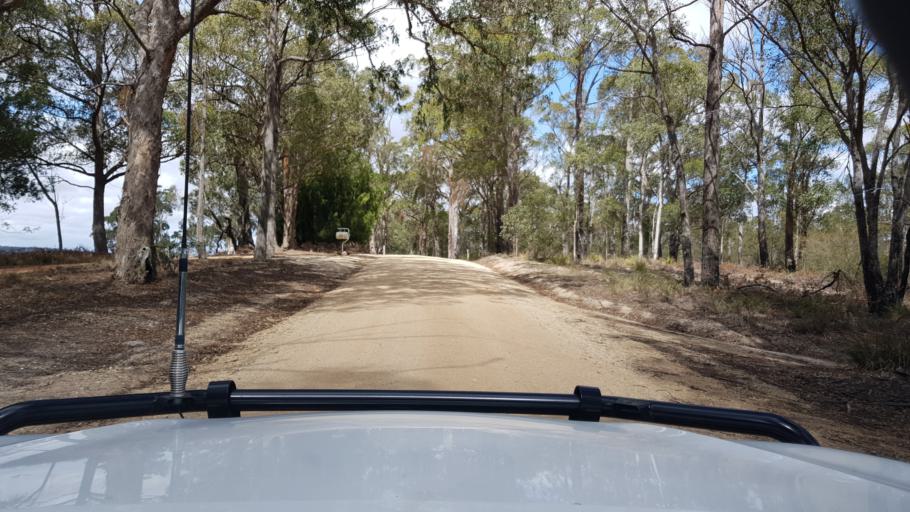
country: AU
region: Victoria
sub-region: East Gippsland
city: Bairnsdale
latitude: -37.7510
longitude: 147.6074
